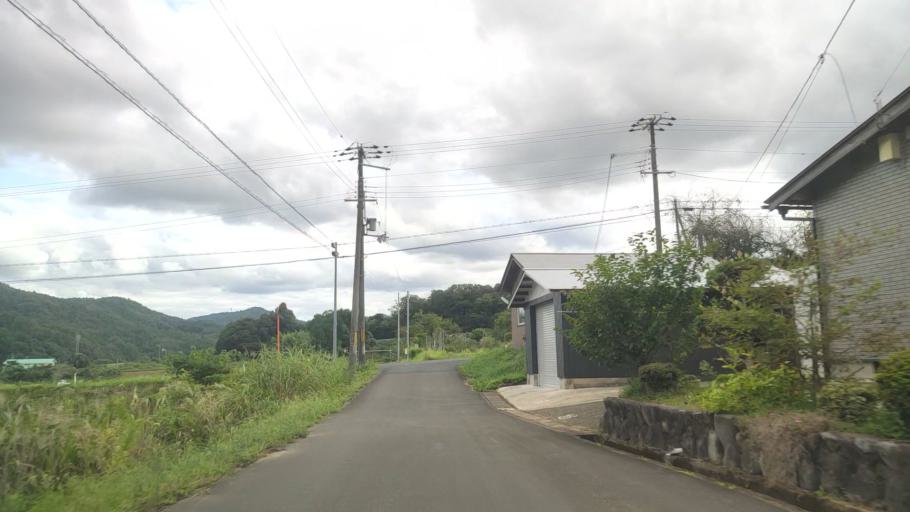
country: JP
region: Hyogo
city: Toyooka
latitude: 35.5982
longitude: 134.8821
